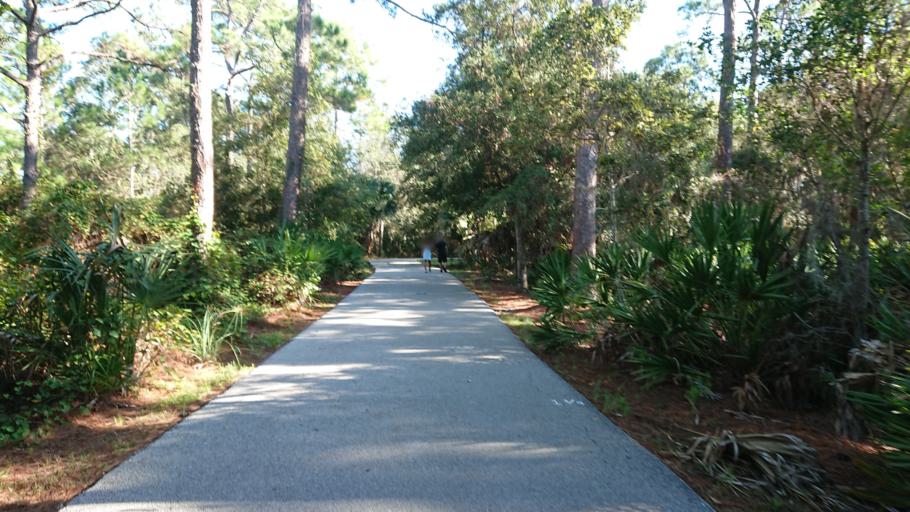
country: US
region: Florida
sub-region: Pinellas County
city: Seminole
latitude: 27.8467
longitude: -82.7755
